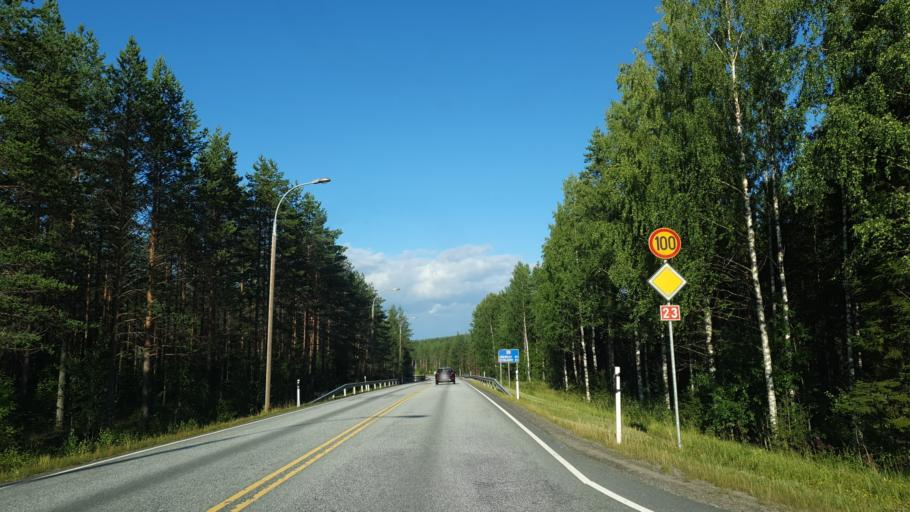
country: FI
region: North Karelia
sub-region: Joensuu
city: Outokumpu
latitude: 62.5221
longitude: 29.0435
